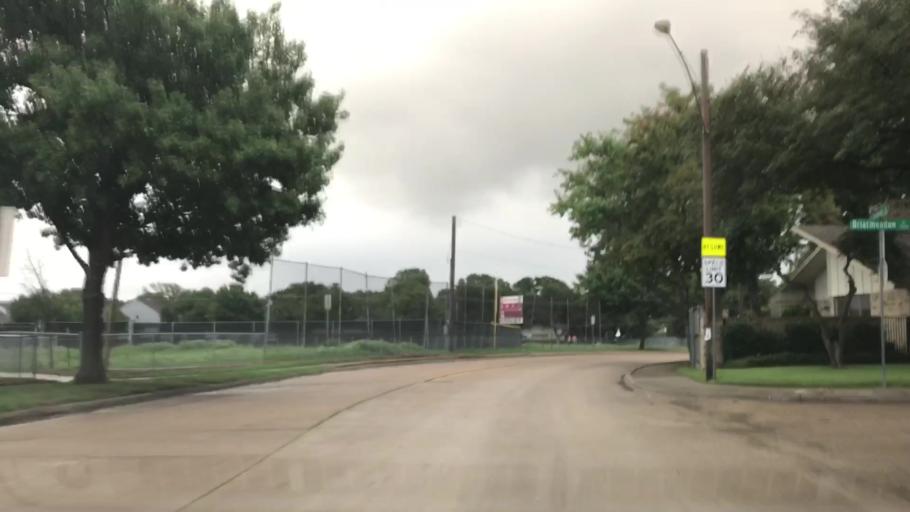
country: US
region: Texas
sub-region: Dallas County
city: University Park
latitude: 32.8822
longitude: -96.7846
